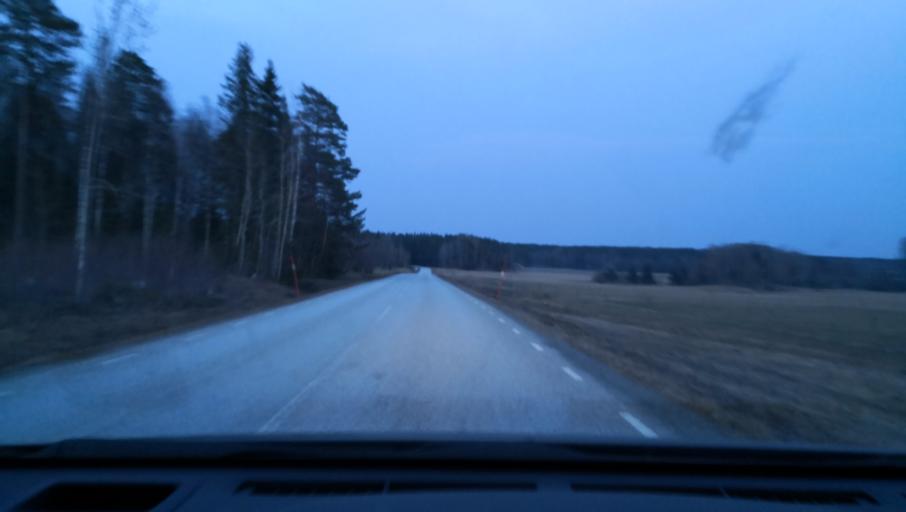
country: SE
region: OErebro
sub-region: Lindesbergs Kommun
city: Lindesberg
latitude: 59.5940
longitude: 15.2986
